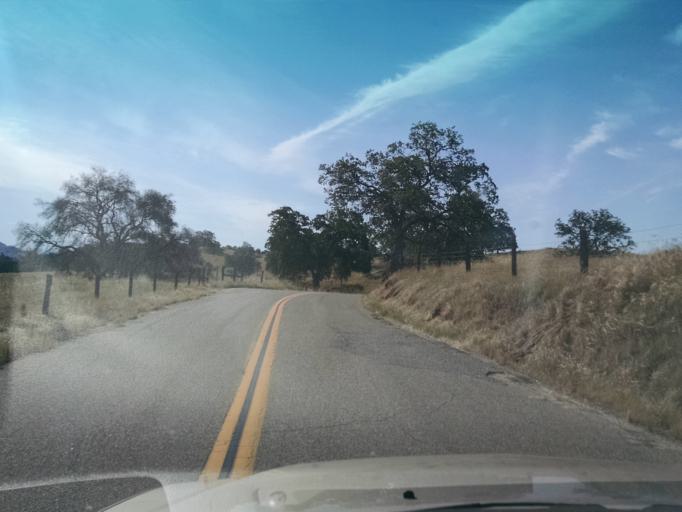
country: US
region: California
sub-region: Madera County
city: Yosemite Lakes
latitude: 37.1167
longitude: -119.6972
